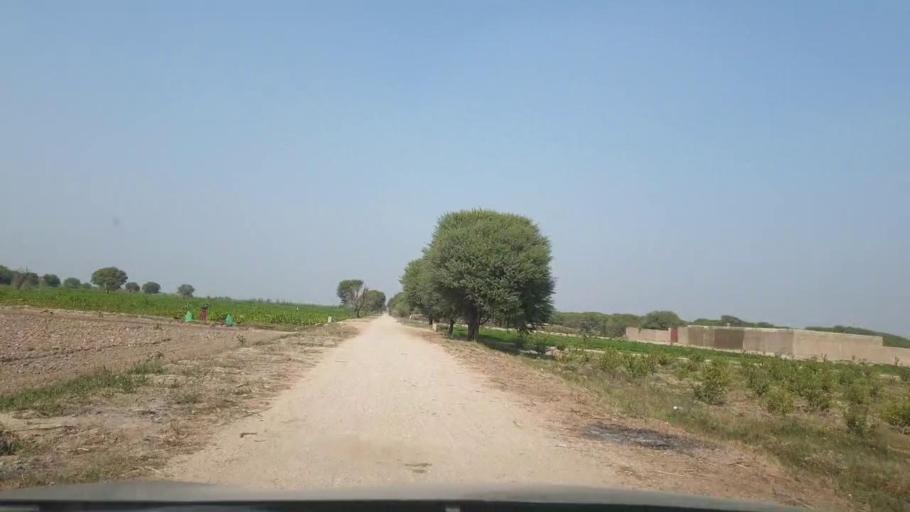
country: PK
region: Sindh
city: Tando Allahyar
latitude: 25.5630
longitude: 68.8255
